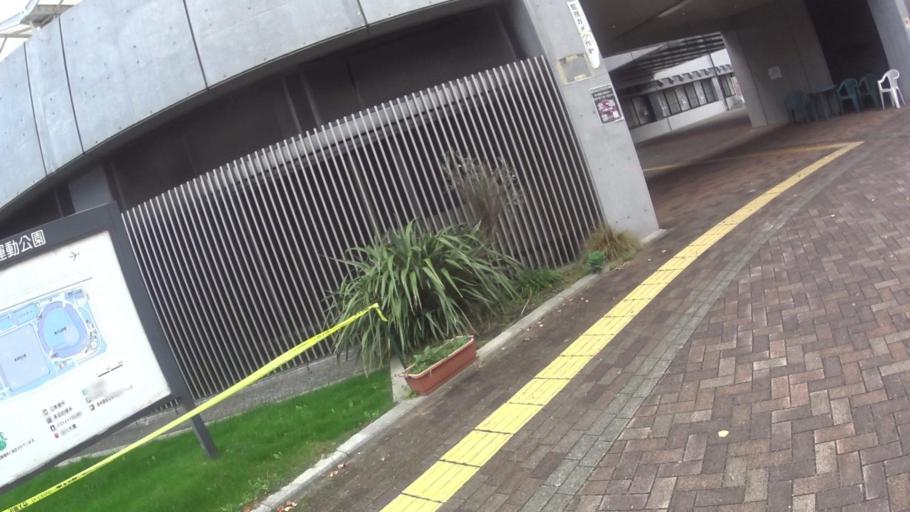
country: JP
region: Shiga Prefecture
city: Otsu-shi
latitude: 35.0211
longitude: 135.8578
